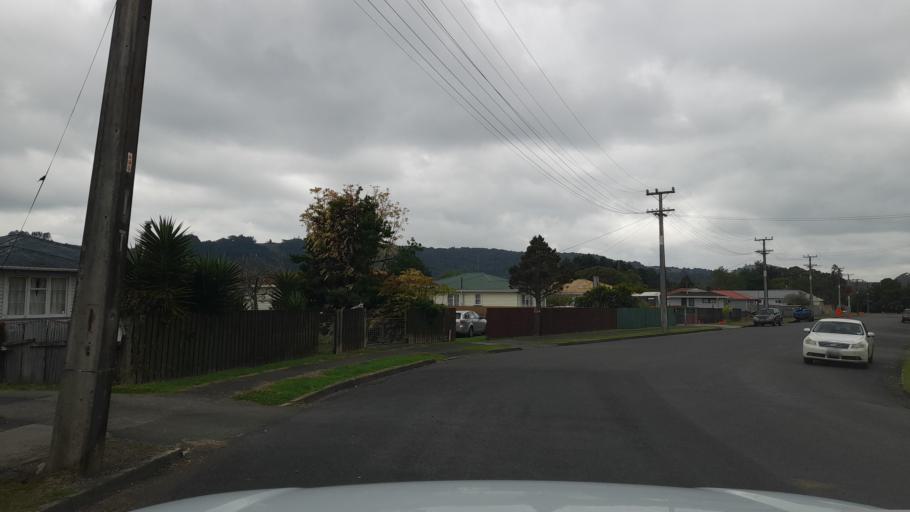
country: NZ
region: Northland
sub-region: Far North District
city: Waimate North
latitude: -35.4047
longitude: 173.7927
